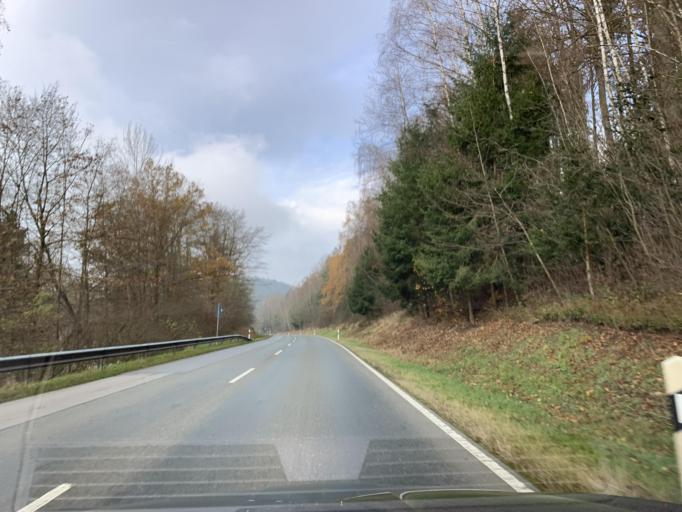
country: DE
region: Bavaria
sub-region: Upper Palatinate
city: Roetz
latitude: 49.3488
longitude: 12.4908
